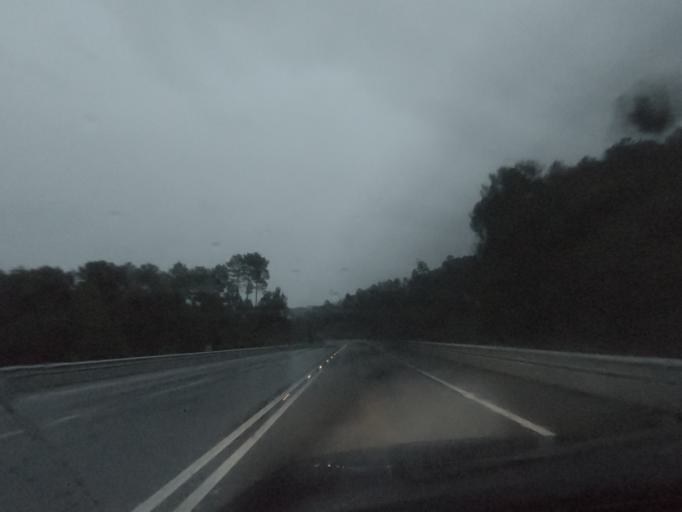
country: PT
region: Vila Real
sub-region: Vila Real
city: Vila Real
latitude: 41.2677
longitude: -7.6767
